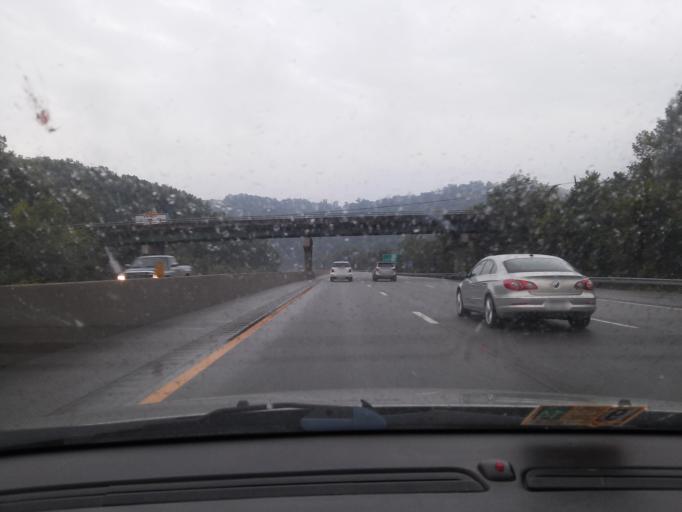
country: US
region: West Virginia
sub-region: Kanawha County
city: Nitro
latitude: 38.4345
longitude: -81.8270
